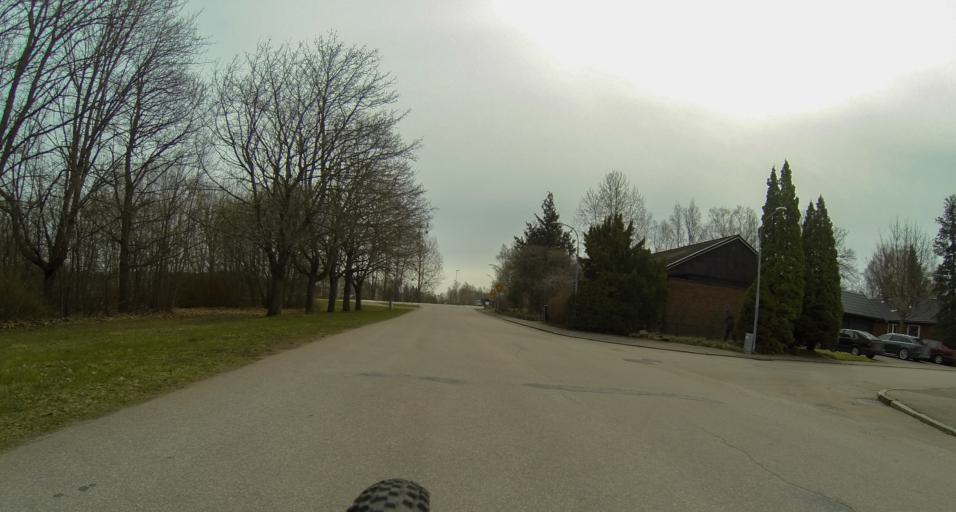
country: SE
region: Vaestmanland
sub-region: Vasteras
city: Vasteras
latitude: 59.5945
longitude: 16.6105
